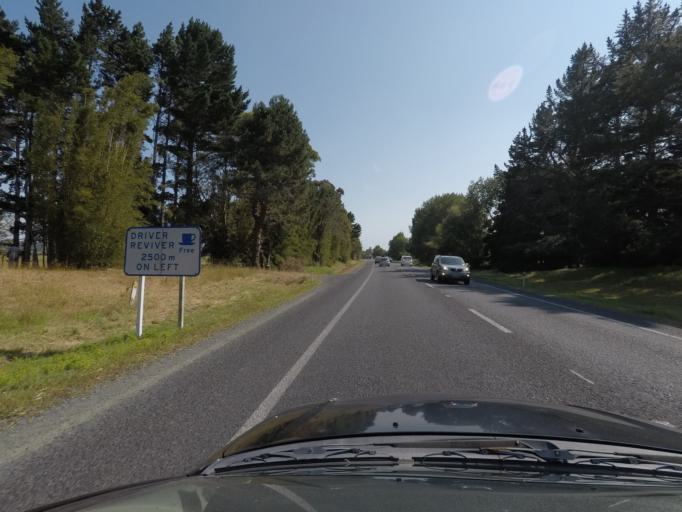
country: NZ
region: Northland
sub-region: Whangarei
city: Ruakaka
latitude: -35.9568
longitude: 174.4510
